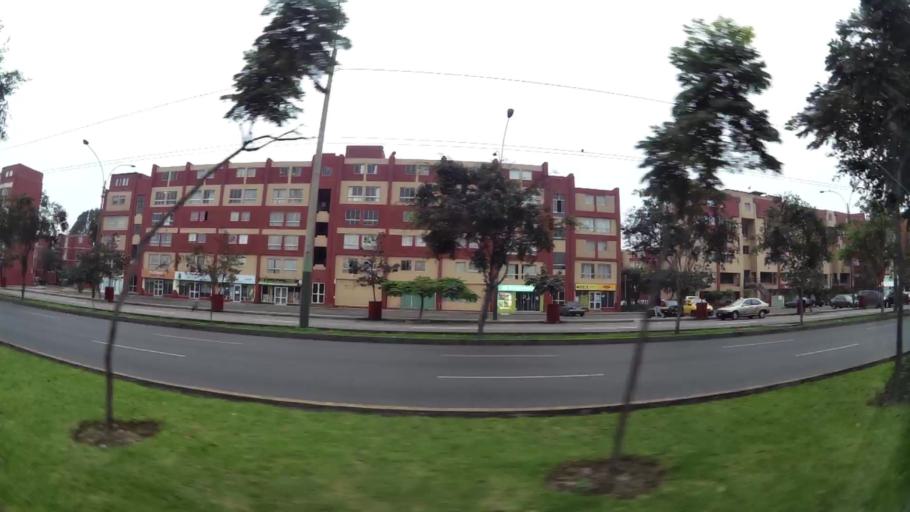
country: PE
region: Lima
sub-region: Lima
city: Surco
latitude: -12.1121
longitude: -77.0045
